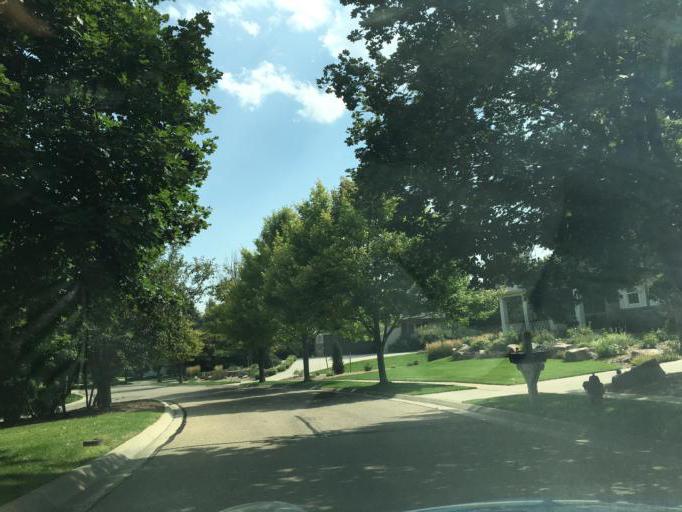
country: US
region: Colorado
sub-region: Boulder County
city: Lafayette
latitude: 40.0212
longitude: -105.1183
